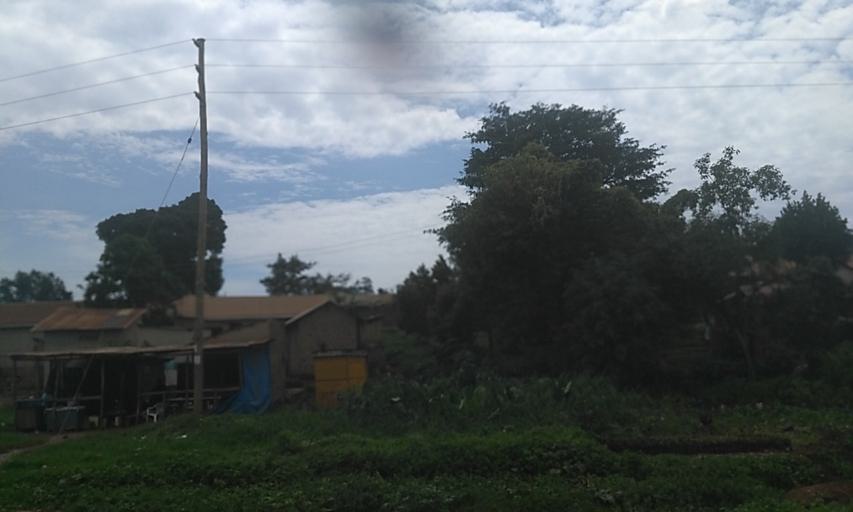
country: UG
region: Central Region
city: Kampala Central Division
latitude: 0.3445
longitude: 32.5413
